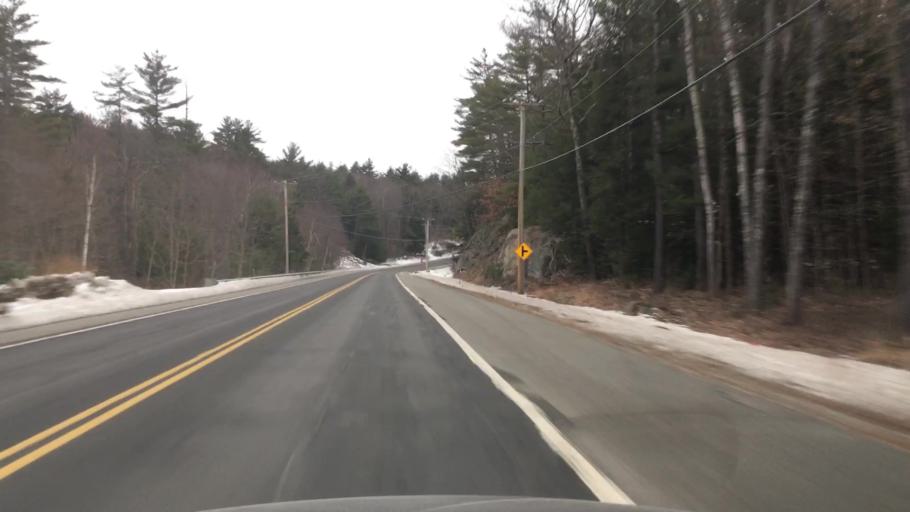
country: US
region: New Hampshire
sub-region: Merrimack County
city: Sutton
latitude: 43.2394
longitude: -71.9186
